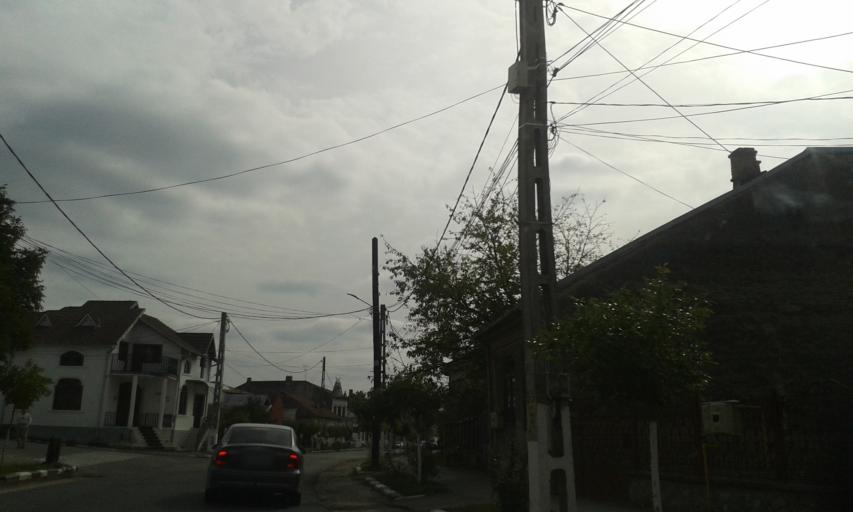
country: RO
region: Gorj
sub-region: Comuna Targu Carbunesti
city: Targu Carbunesti
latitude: 44.9558
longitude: 23.5134
